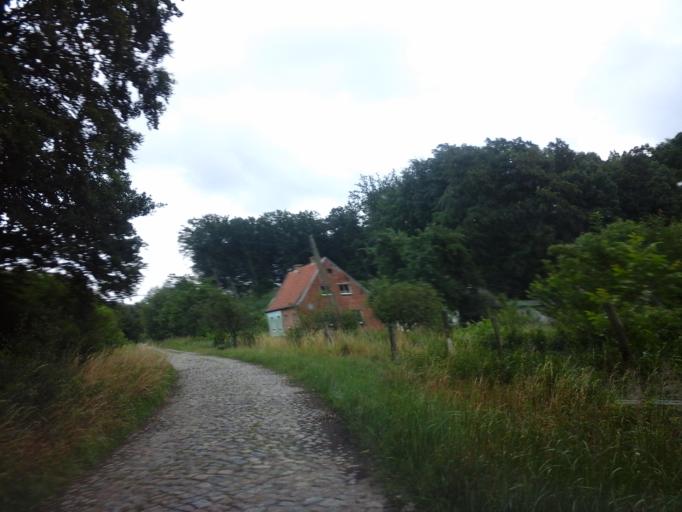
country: PL
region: West Pomeranian Voivodeship
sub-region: Powiat choszczenski
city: Krzecin
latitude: 53.0108
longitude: 15.4646
